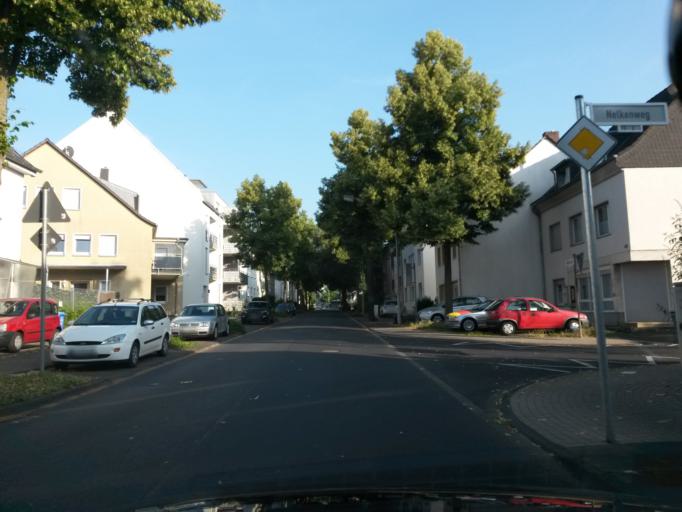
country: DE
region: North Rhine-Westphalia
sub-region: Regierungsbezirk Koln
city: Alfter
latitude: 50.7181
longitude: 7.0431
